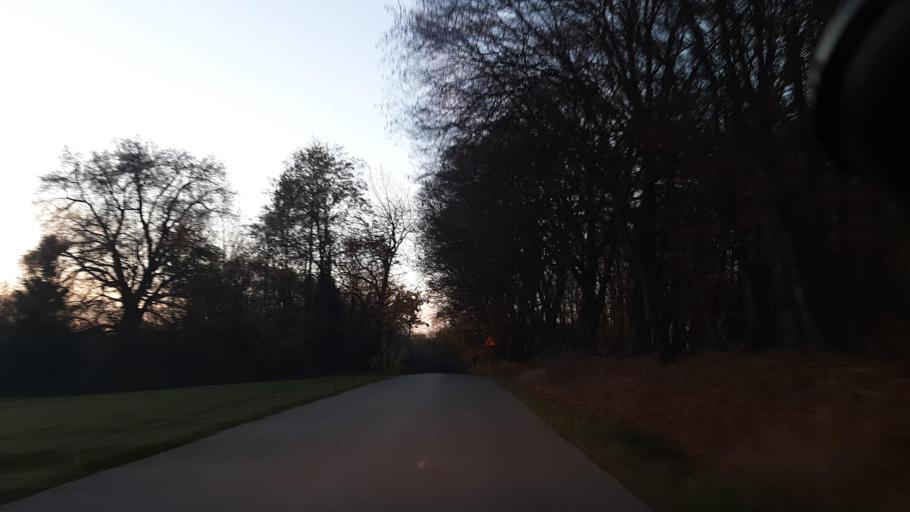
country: PL
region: Lublin Voivodeship
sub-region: Powiat lubelski
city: Jastkow
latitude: 51.3406
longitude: 22.4153
